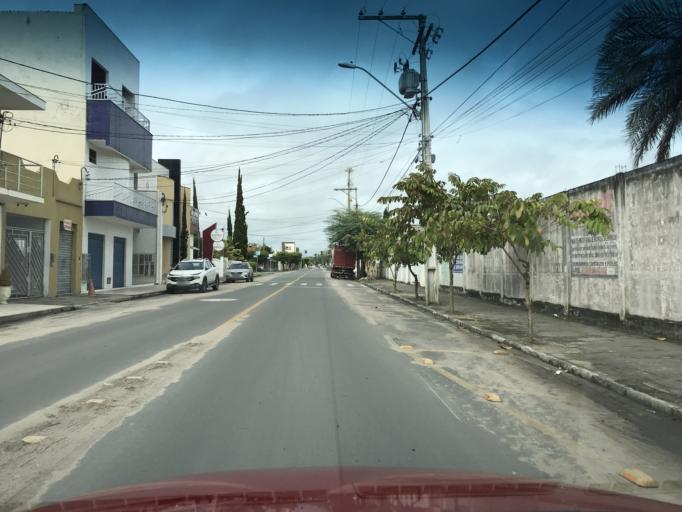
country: BR
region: Bahia
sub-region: Cruz Das Almas
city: Cruz das Almas
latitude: -12.6703
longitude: -39.1027
